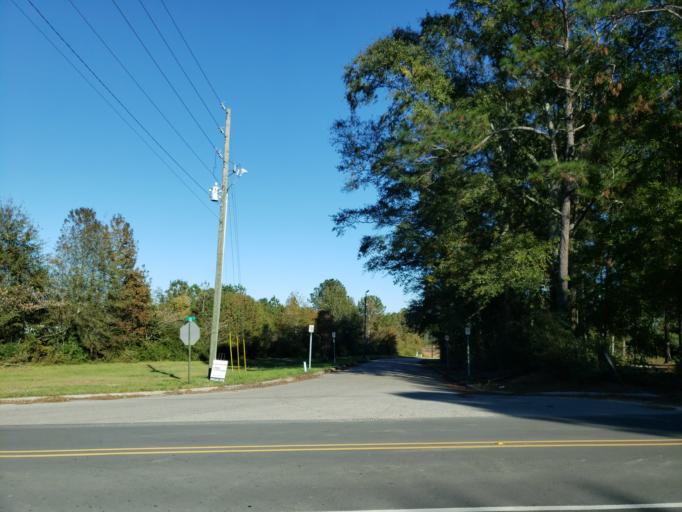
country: US
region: Mississippi
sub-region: Lamar County
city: West Hattiesburg
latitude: 31.2555
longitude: -89.3384
